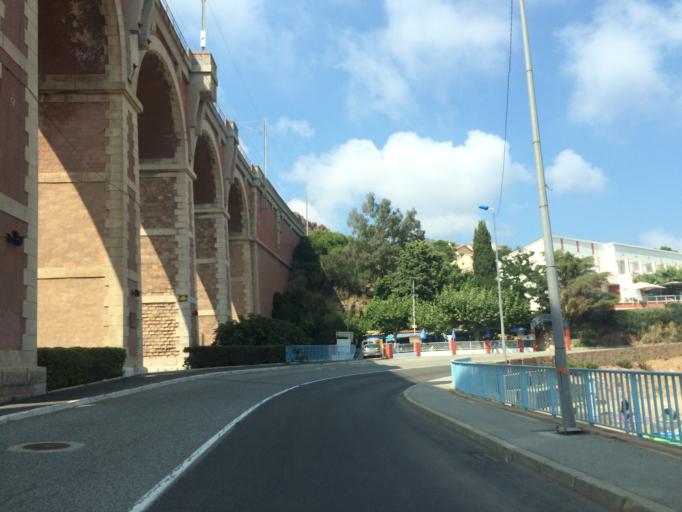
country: FR
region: Provence-Alpes-Cote d'Azur
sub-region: Departement des Alpes-Maritimes
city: Theoule-sur-Mer
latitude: 43.4374
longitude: 6.8921
